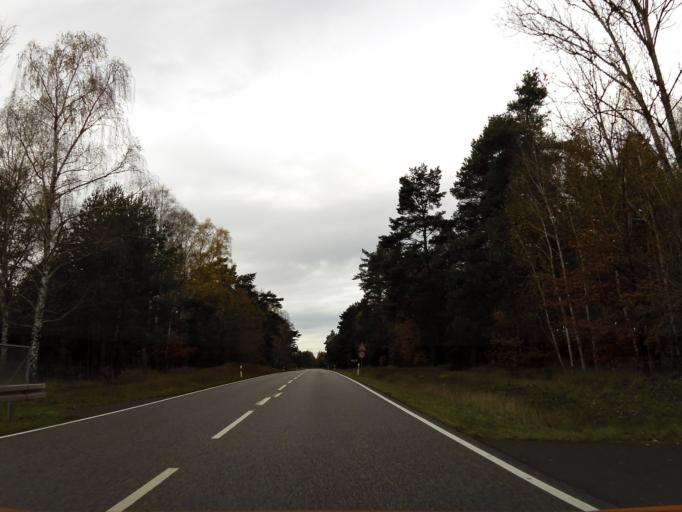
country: DE
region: Saxony-Anhalt
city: Colbitz
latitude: 52.3560
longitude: 11.5410
